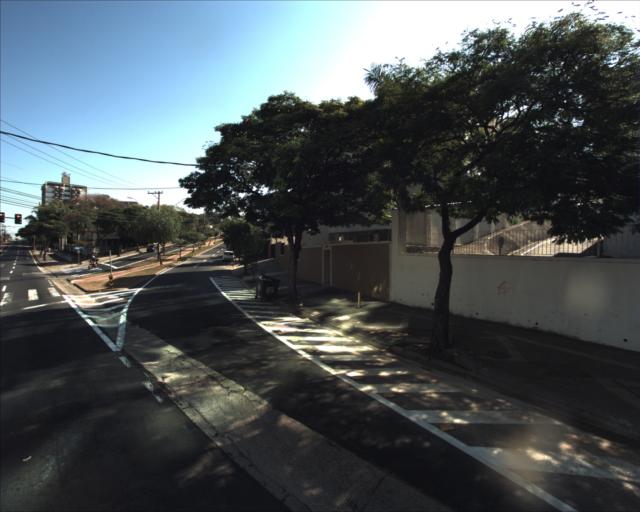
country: BR
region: Sao Paulo
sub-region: Sorocaba
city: Sorocaba
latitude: -23.4911
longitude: -47.4717
